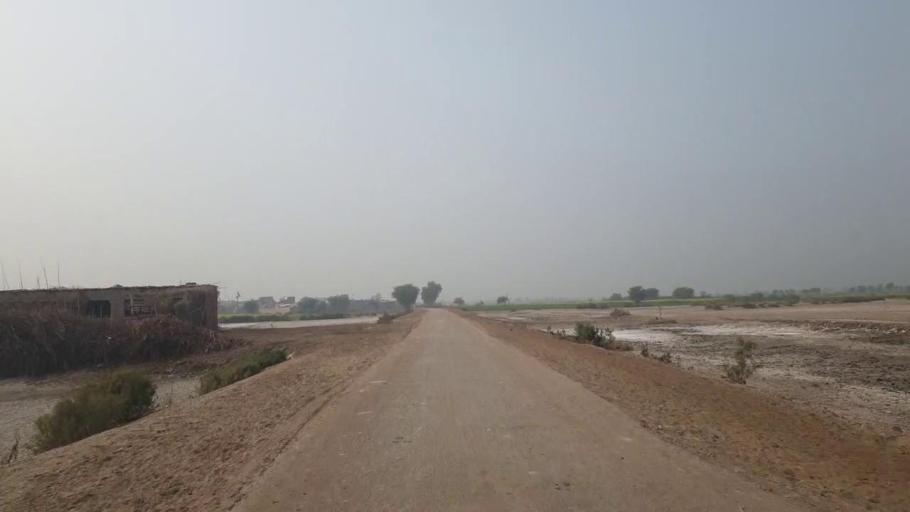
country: PK
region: Sindh
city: Shahdadpur
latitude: 25.8460
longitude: 68.5771
